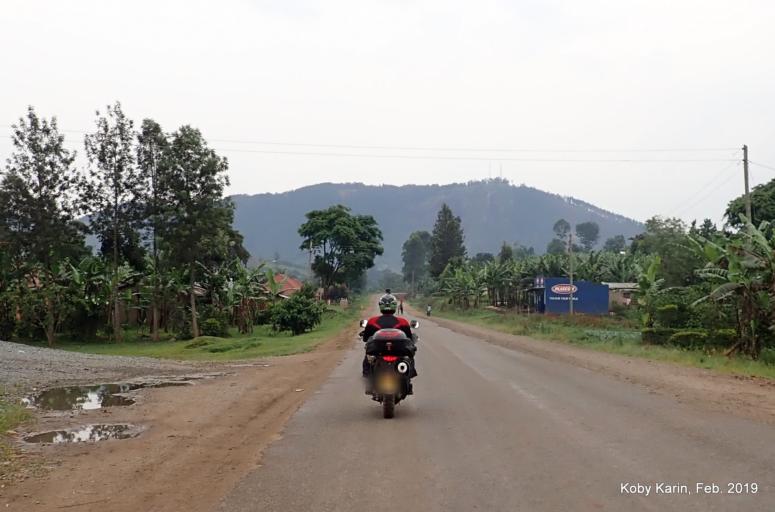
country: UG
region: Western Region
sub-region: Rubirizi District
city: Rubirizi
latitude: -0.2942
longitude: 30.1040
